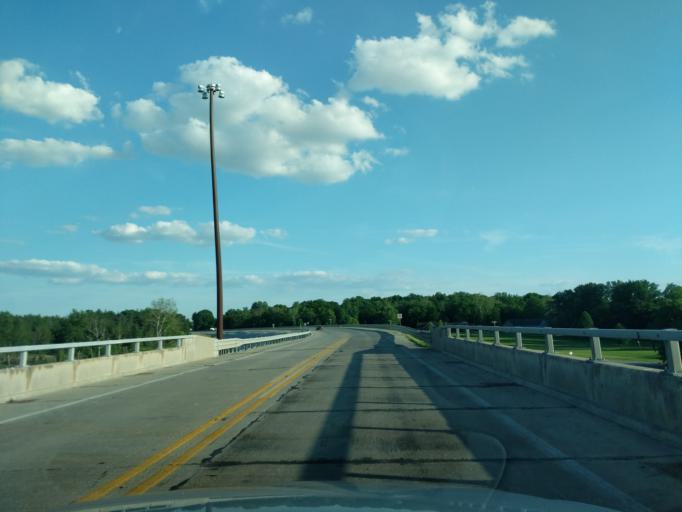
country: US
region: Indiana
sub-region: Huntington County
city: Huntington
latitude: 40.8455
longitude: -85.4687
